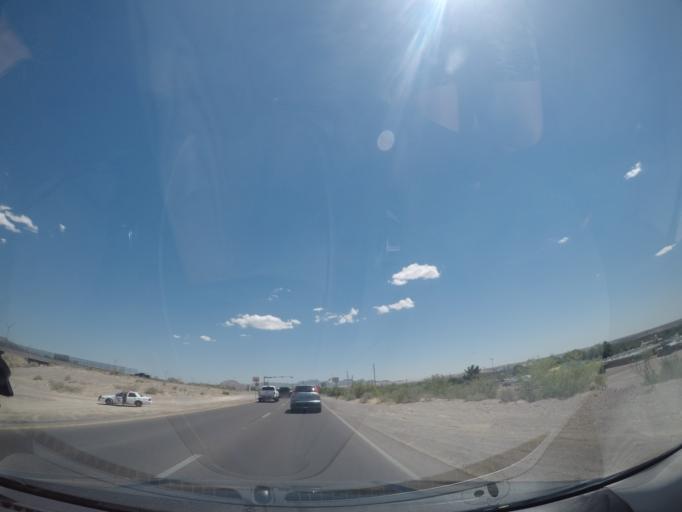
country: US
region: New Mexico
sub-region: Dona Ana County
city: Sunland Park
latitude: 31.8533
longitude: -106.5756
